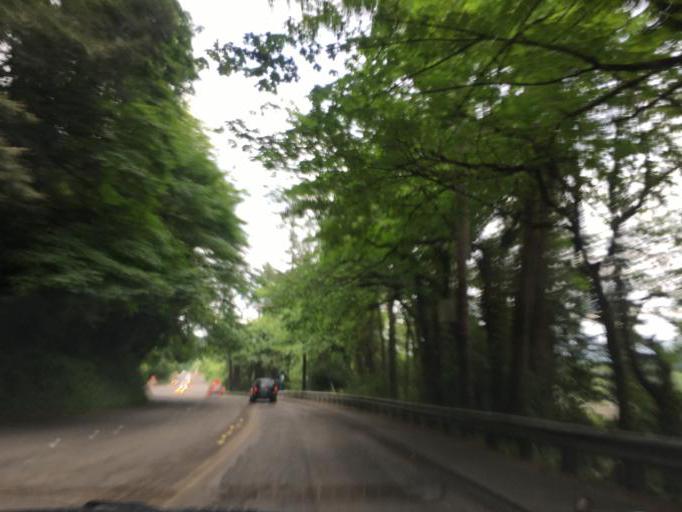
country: US
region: Oregon
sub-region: Clackamas County
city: Milwaukie
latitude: 45.4464
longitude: -122.6569
